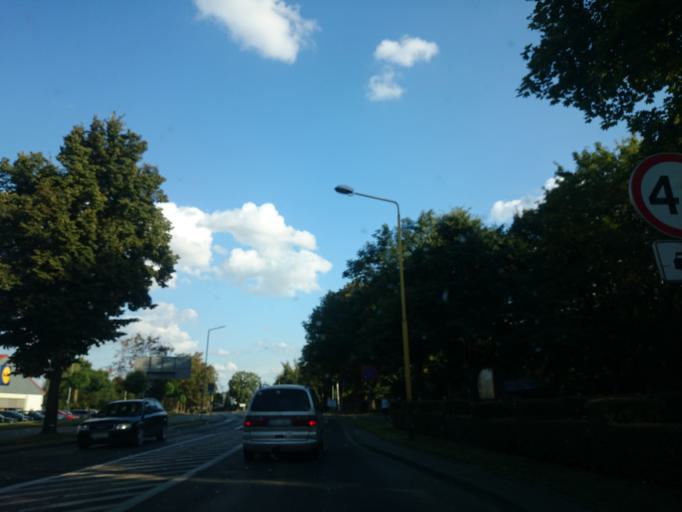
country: PL
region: West Pomeranian Voivodeship
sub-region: Powiat pyrzycki
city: Pyrzyce
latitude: 53.1392
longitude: 14.8918
